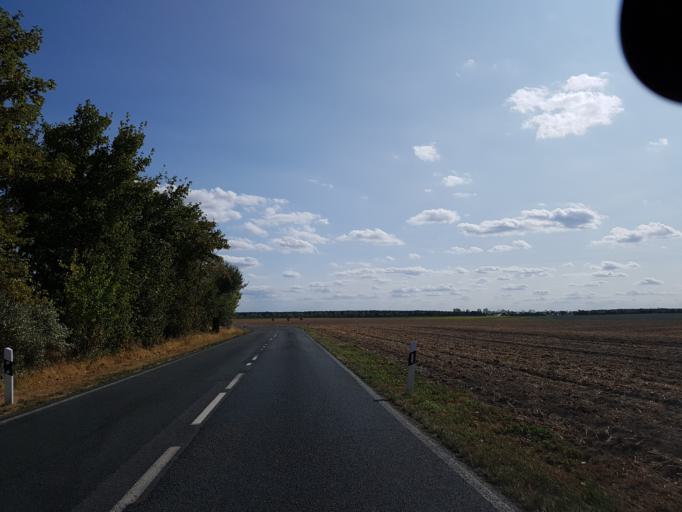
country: DE
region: Saxony-Anhalt
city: Zahna
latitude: 51.9837
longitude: 12.8585
